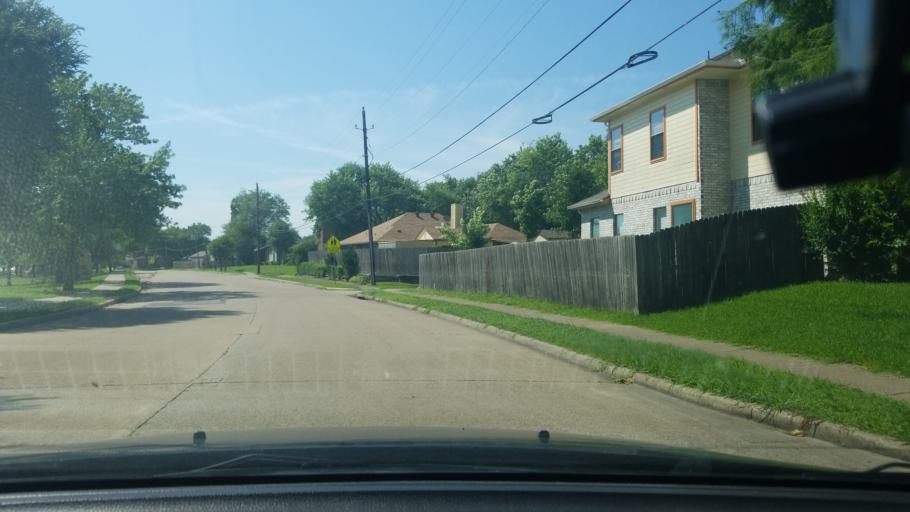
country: US
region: Texas
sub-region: Dallas County
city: Mesquite
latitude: 32.7740
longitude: -96.5825
